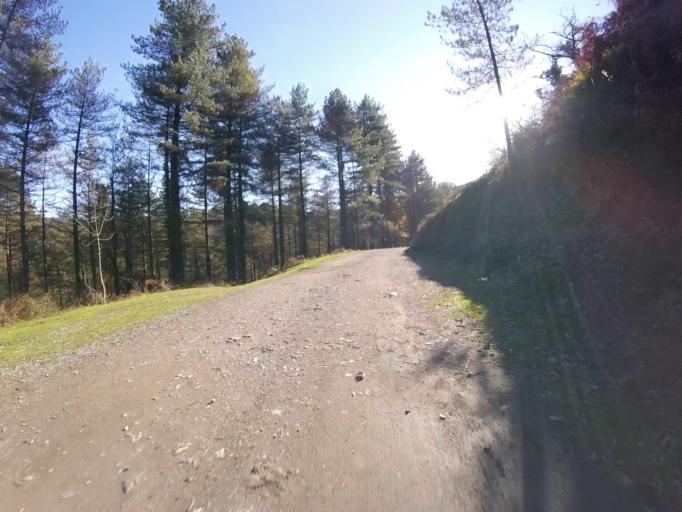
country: ES
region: Navarre
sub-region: Provincia de Navarra
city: Bera
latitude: 43.3146
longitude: -1.6906
